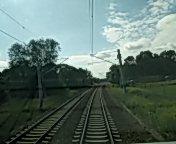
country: DE
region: Brandenburg
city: Halbe
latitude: 52.0784
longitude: 13.7268
